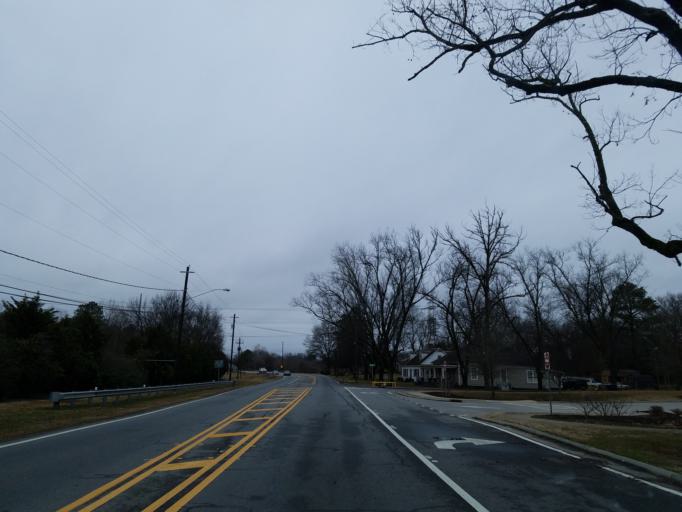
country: US
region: Georgia
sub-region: Bartow County
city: Cartersville
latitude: 34.1770
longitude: -84.8116
